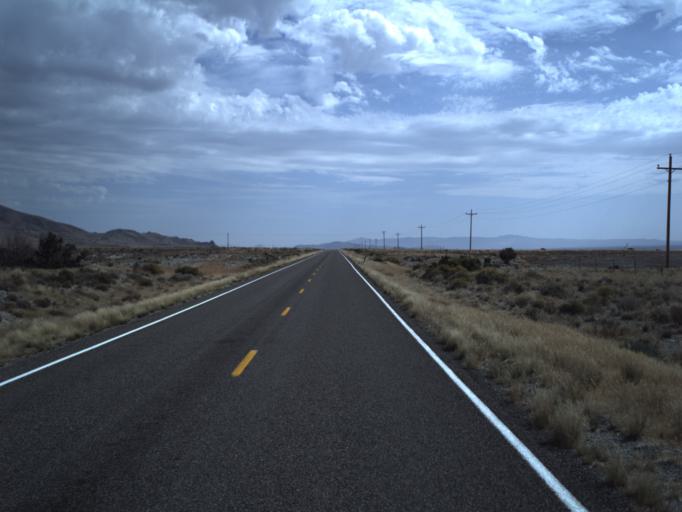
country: US
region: Utah
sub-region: Tooele County
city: Wendover
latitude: 41.4342
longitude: -113.7682
